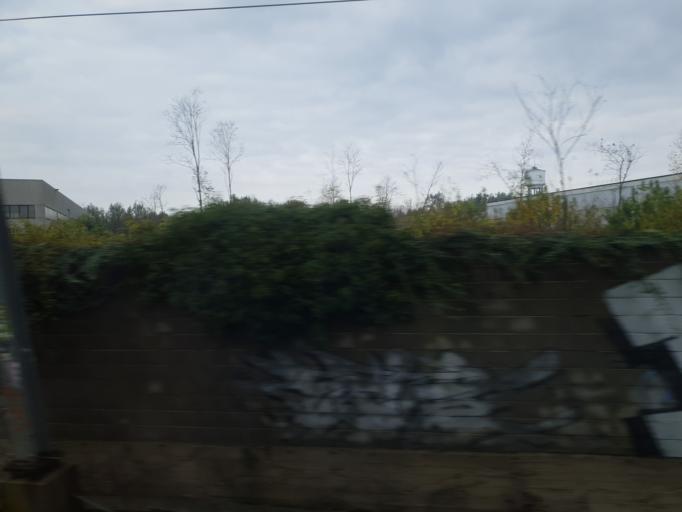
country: IT
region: Lombardy
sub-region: Citta metropolitana di Milano
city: Rescaldina
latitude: 45.6214
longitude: 8.9365
